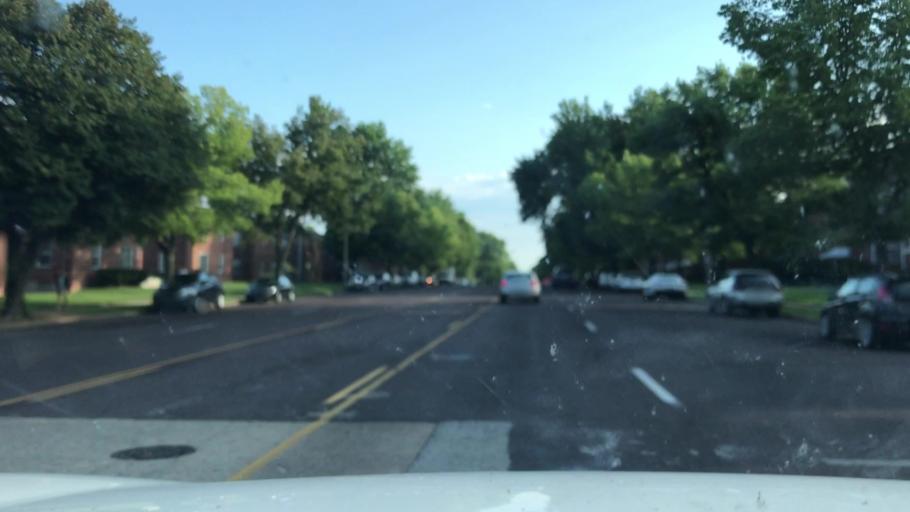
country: US
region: Missouri
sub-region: Saint Louis County
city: Maplewood
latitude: 38.5932
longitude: -90.3095
